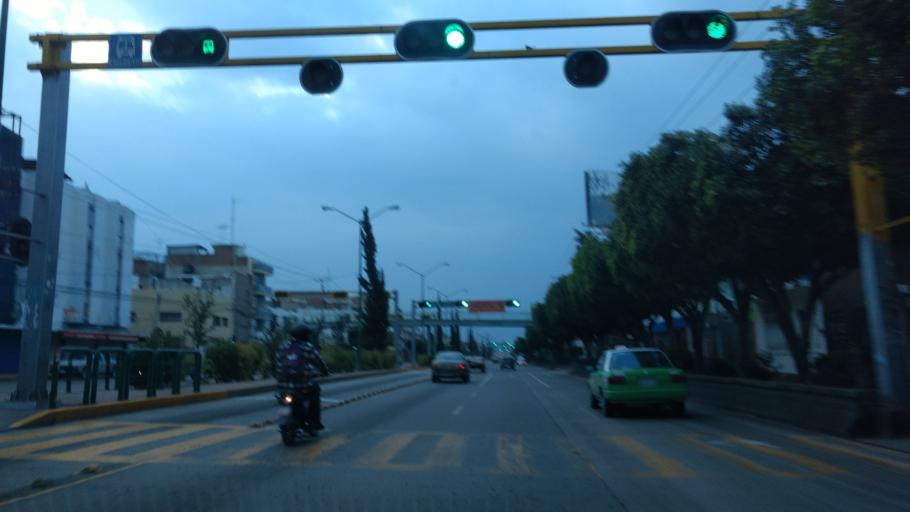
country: MX
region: Guanajuato
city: Leon
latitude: 21.1235
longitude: -101.6770
